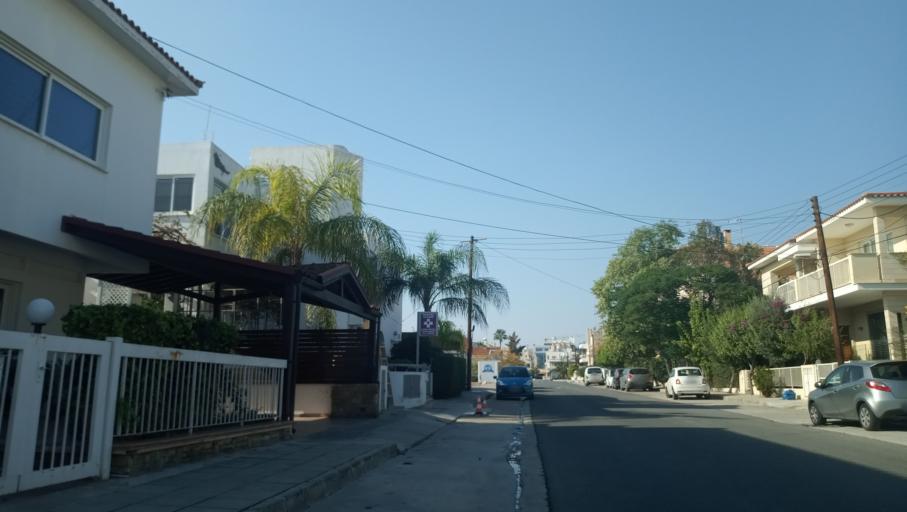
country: CY
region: Lefkosia
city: Nicosia
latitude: 35.1434
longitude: 33.3792
